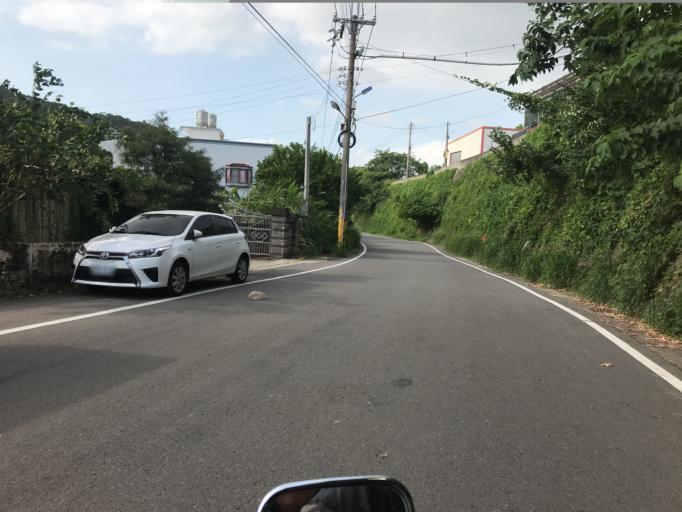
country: TW
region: Taiwan
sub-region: Hsinchu
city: Hsinchu
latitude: 24.7782
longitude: 120.9321
